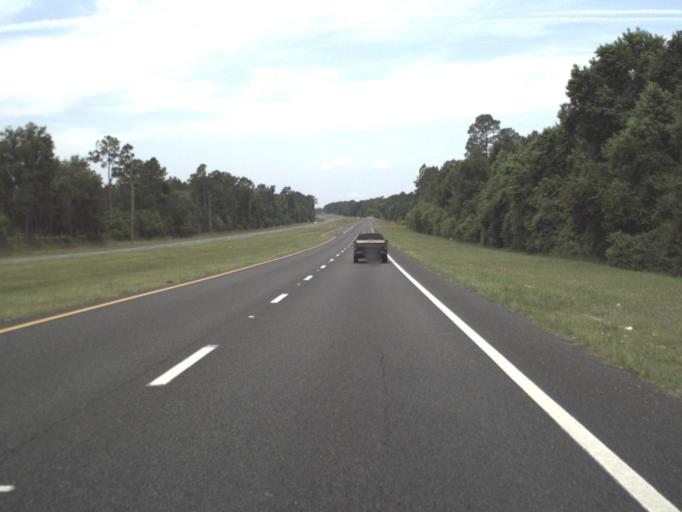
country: US
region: Florida
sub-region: Alachua County
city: Hawthorne
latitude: 29.5998
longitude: -82.1348
